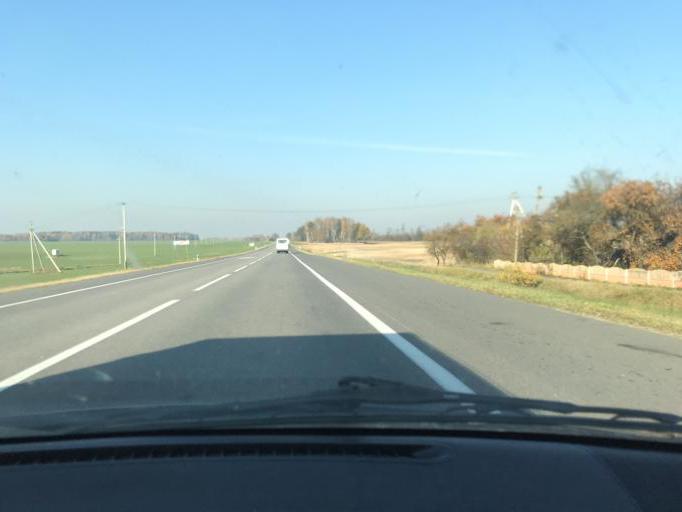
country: BY
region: Vitebsk
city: Balbasava
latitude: 54.3169
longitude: 30.4473
